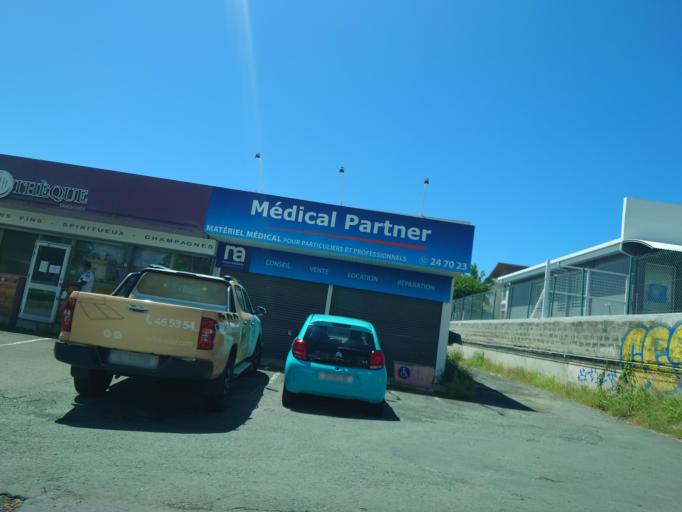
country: NC
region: South Province
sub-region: Noumea
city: Noumea
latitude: -22.2682
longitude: 166.4621
